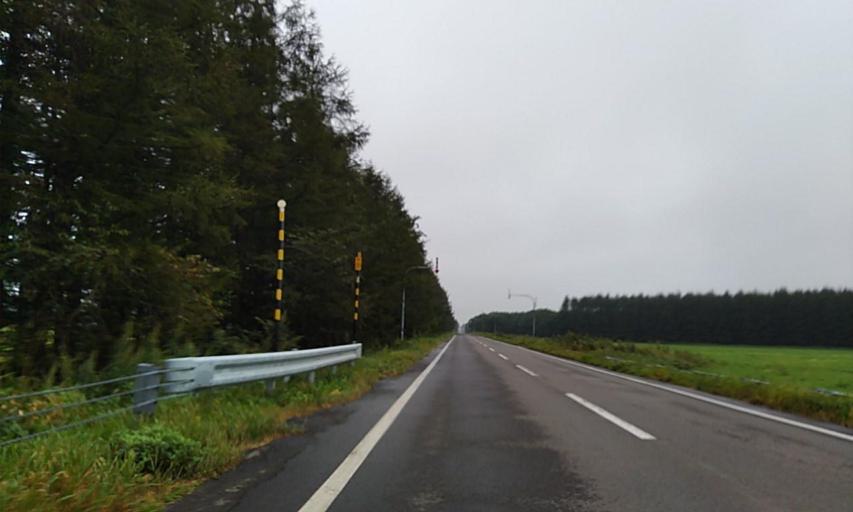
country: JP
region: Hokkaido
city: Shibetsu
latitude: 43.5225
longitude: 144.6881
